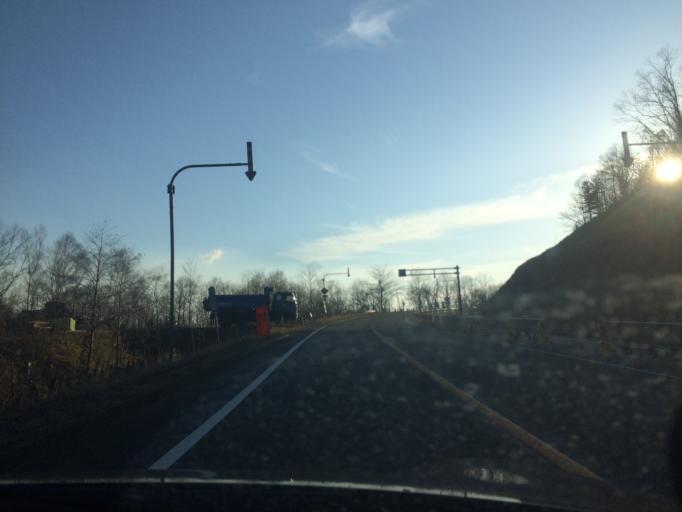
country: JP
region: Hokkaido
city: Otofuke
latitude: 42.9748
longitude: 142.7990
